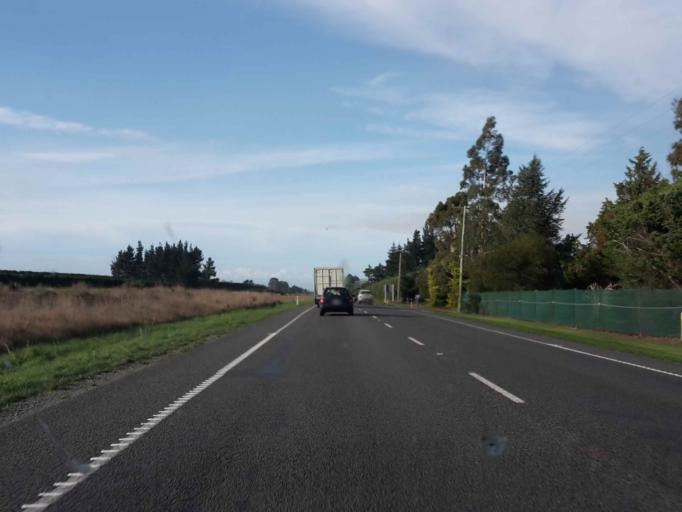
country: NZ
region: Canterbury
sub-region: Ashburton District
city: Tinwald
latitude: -43.9377
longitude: 171.6877
